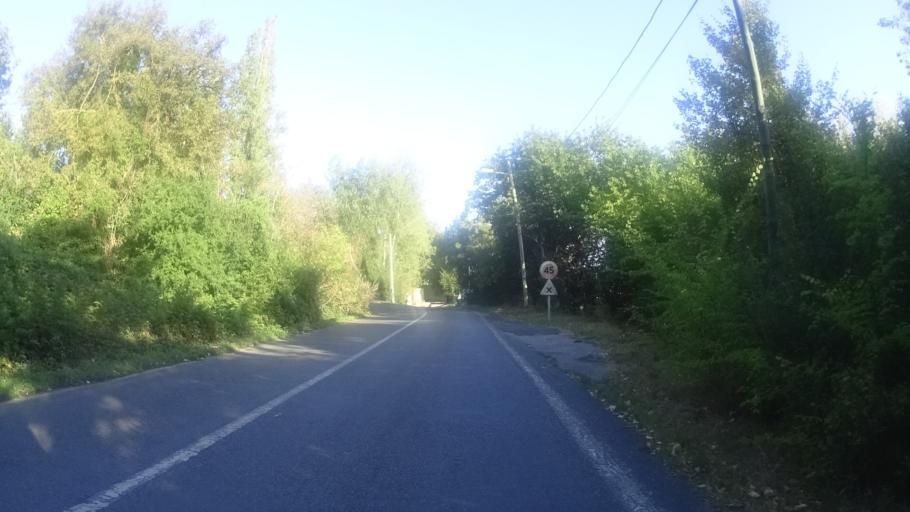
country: FR
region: Ile-de-France
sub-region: Departement de l'Essonne
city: Evry
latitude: 48.6334
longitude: 2.4574
